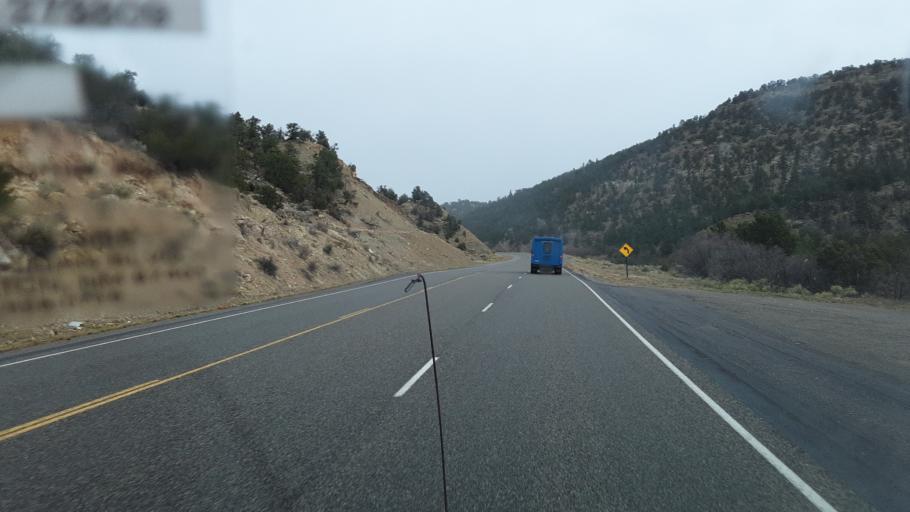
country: US
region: New Mexico
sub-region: Rio Arriba County
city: Tierra Amarilla
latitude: 36.4121
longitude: -106.4842
